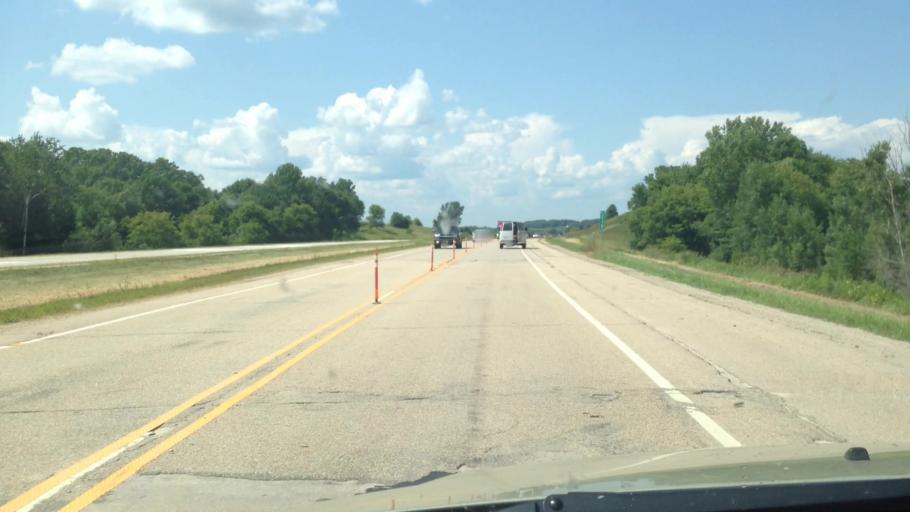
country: US
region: Wisconsin
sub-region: Shawano County
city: Bonduel
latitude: 44.7062
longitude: -88.3758
